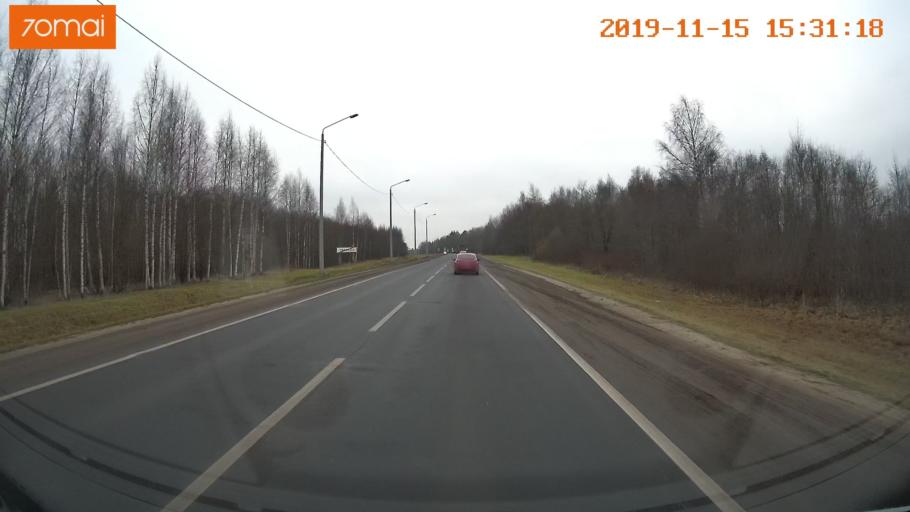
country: RU
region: Jaroslavl
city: Danilov
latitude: 58.1017
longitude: 40.1084
